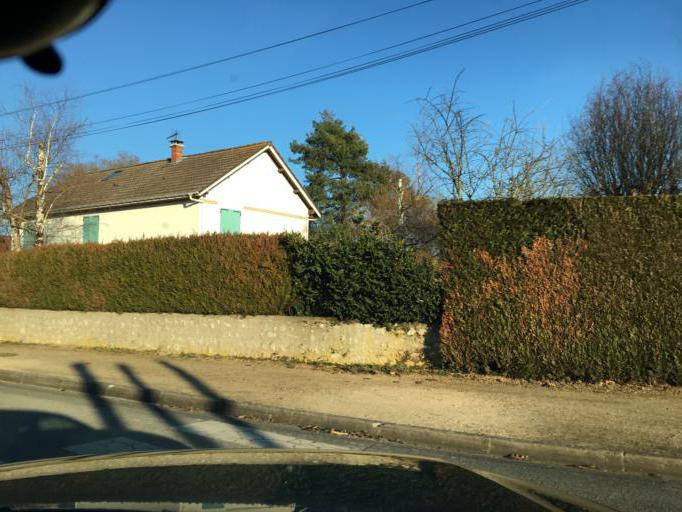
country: FR
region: Centre
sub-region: Departement du Loiret
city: Jouy-le-Potier
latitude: 47.7437
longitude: 1.8124
